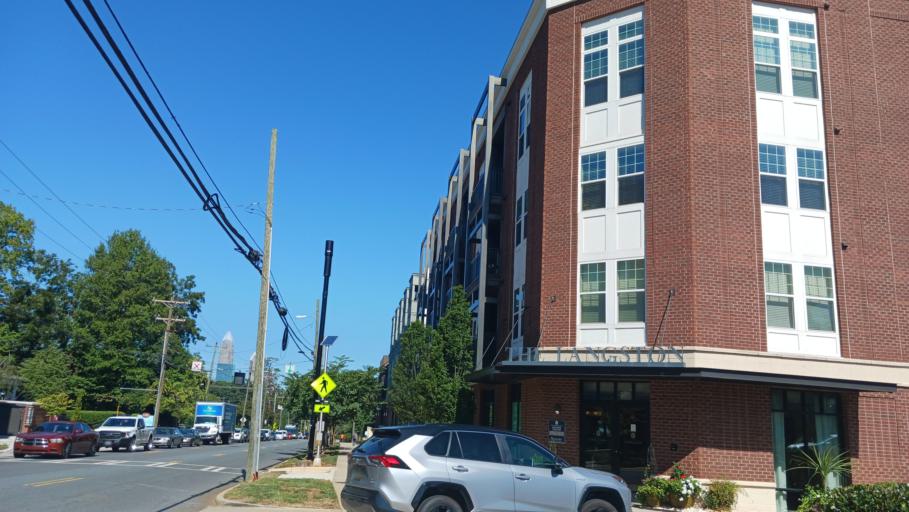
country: US
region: North Carolina
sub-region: Mecklenburg County
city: Charlotte
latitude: 35.2129
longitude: -80.8191
